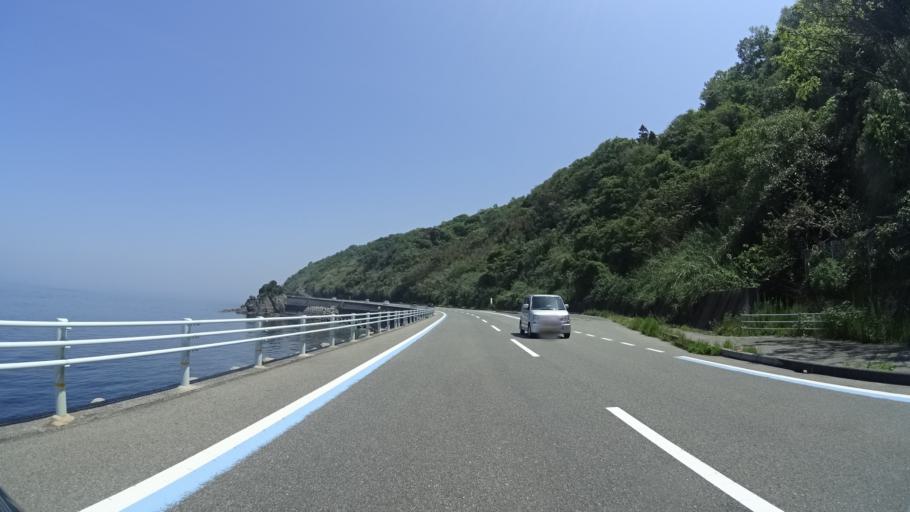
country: JP
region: Ehime
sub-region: Nishiuwa-gun
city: Ikata-cho
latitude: 33.5779
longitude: 132.4447
